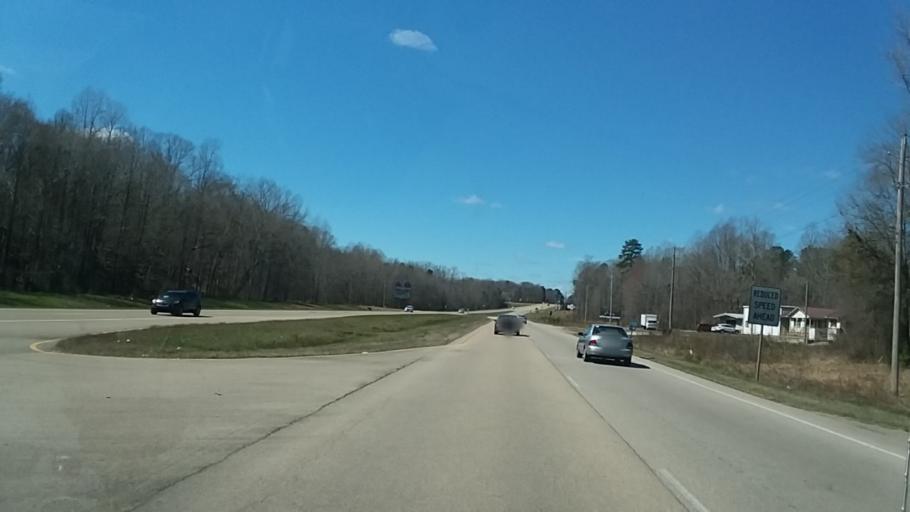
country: US
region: Mississippi
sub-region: Alcorn County
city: Farmington
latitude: 34.8904
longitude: -88.4607
